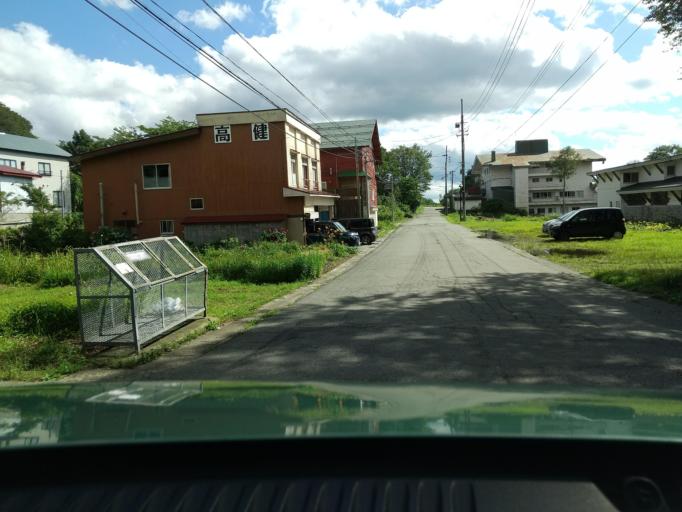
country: JP
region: Iwate
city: Shizukuishi
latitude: 39.7804
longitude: 140.7621
